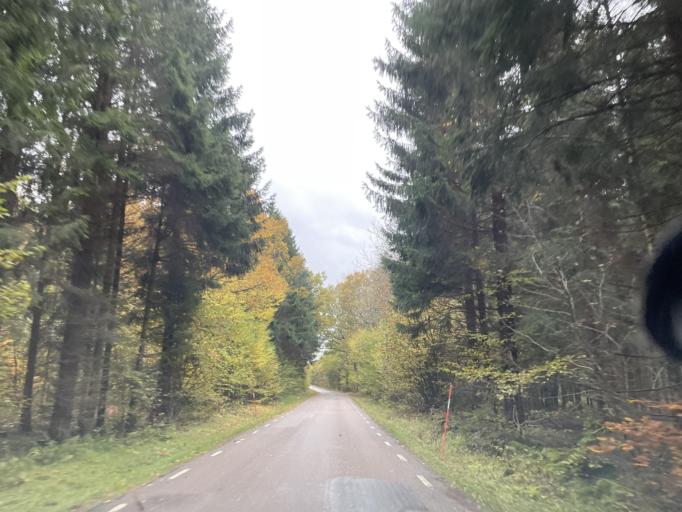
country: SE
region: Skane
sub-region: Svalovs Kommun
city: Kagerod
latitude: 55.9882
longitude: 13.1509
